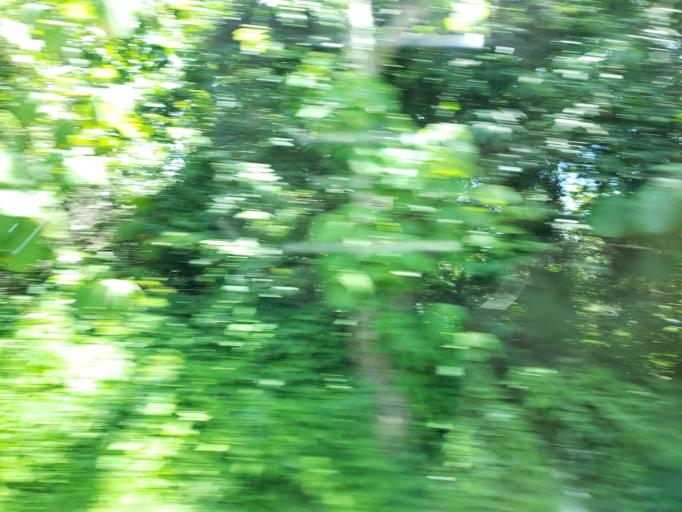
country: ID
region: Bali
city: Kangin
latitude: -8.8325
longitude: 115.1355
